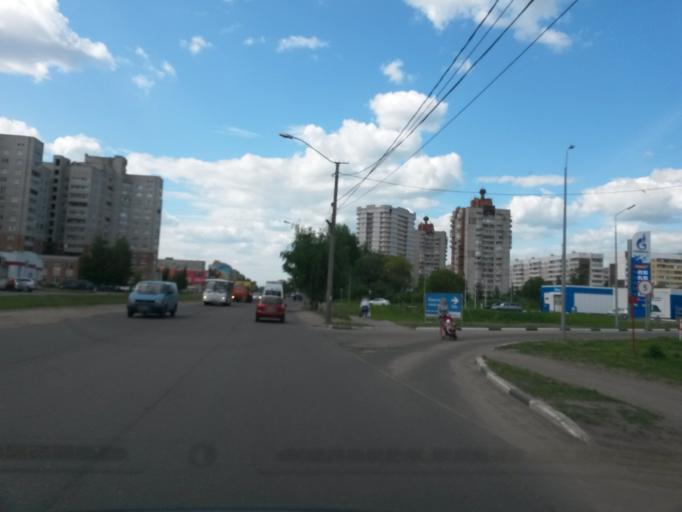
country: RU
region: Jaroslavl
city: Yaroslavl
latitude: 57.6429
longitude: 39.9584
